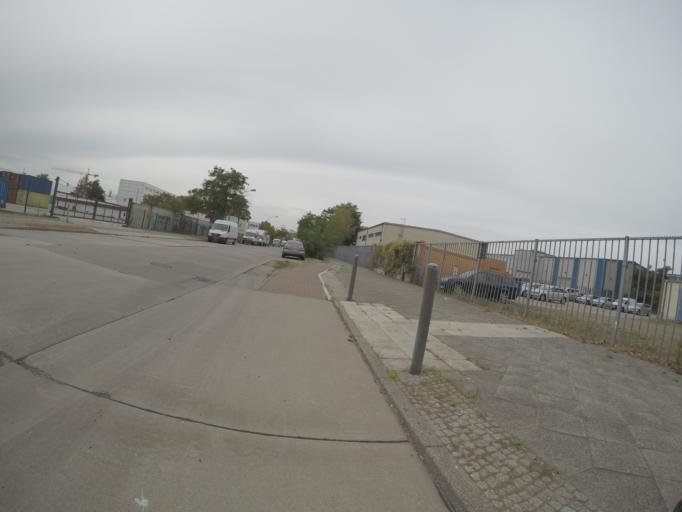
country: DE
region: Berlin
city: Alt-Hohenschoenhausen
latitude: 52.5446
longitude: 13.5230
